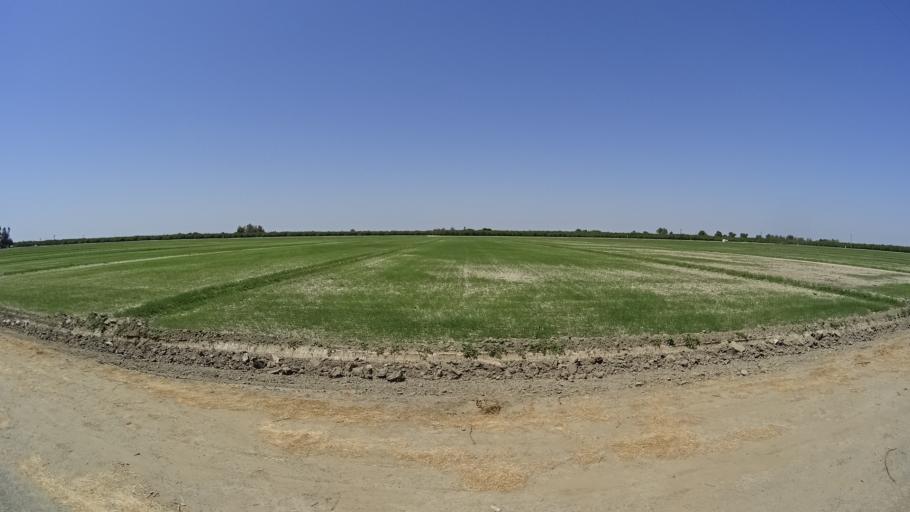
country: US
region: California
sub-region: Kings County
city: Armona
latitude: 36.2732
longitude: -119.7270
